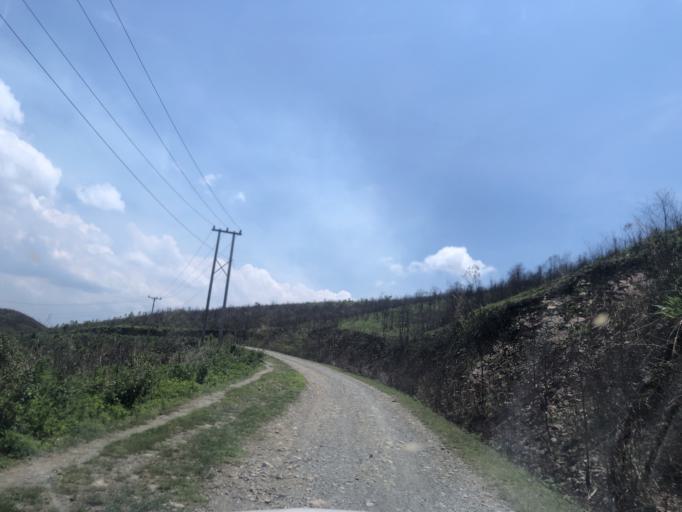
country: LA
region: Phongsali
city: Phongsali
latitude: 21.4195
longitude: 102.1847
